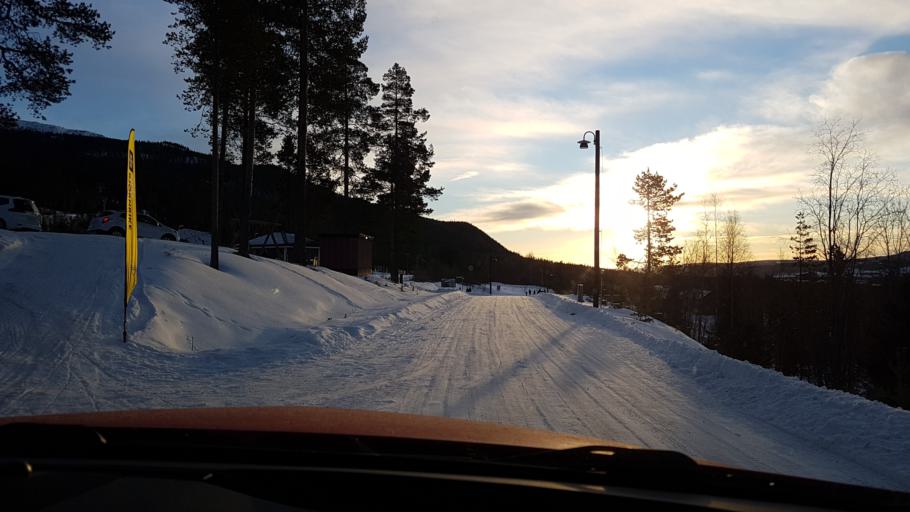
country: SE
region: Jaemtland
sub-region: Harjedalens Kommun
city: Sveg
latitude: 62.4153
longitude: 13.9502
